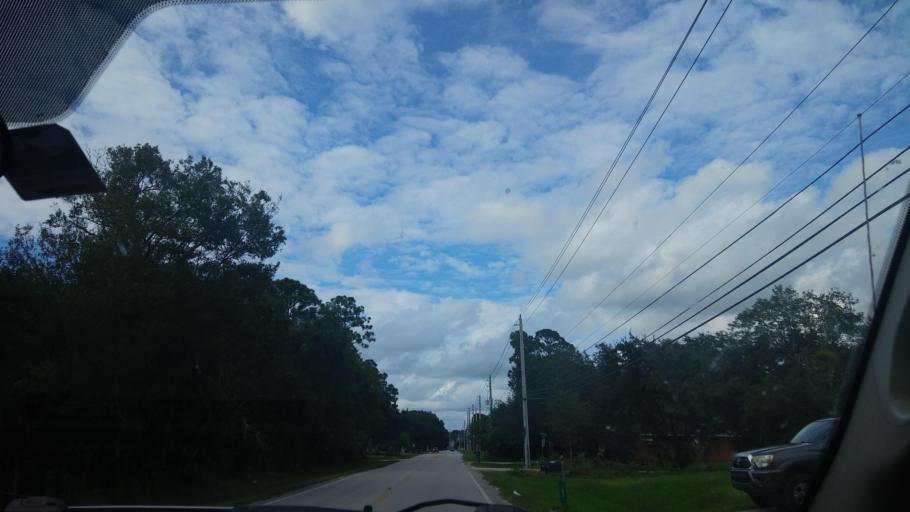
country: US
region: Florida
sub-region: Indian River County
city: Fellsmere
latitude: 27.7651
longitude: -80.5932
